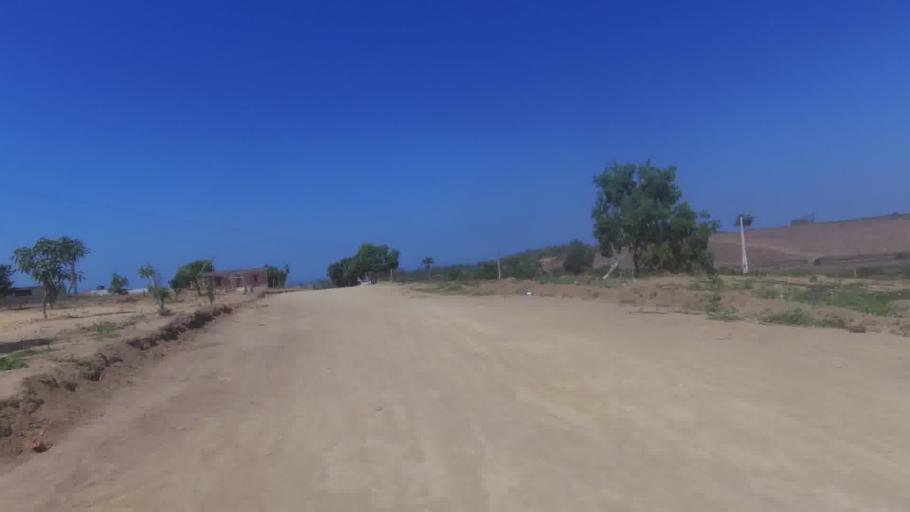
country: BR
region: Espirito Santo
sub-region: Marataizes
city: Marataizes
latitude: -21.1102
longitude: -40.8572
